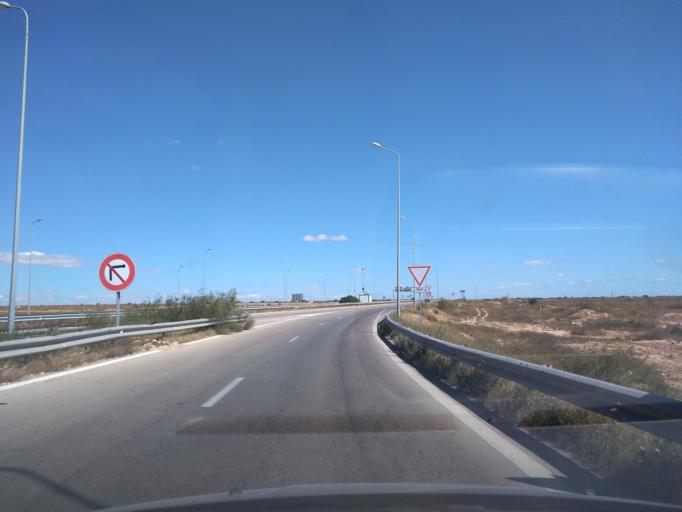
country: TN
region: Safaqis
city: Al Qarmadah
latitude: 34.8920
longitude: 10.7174
